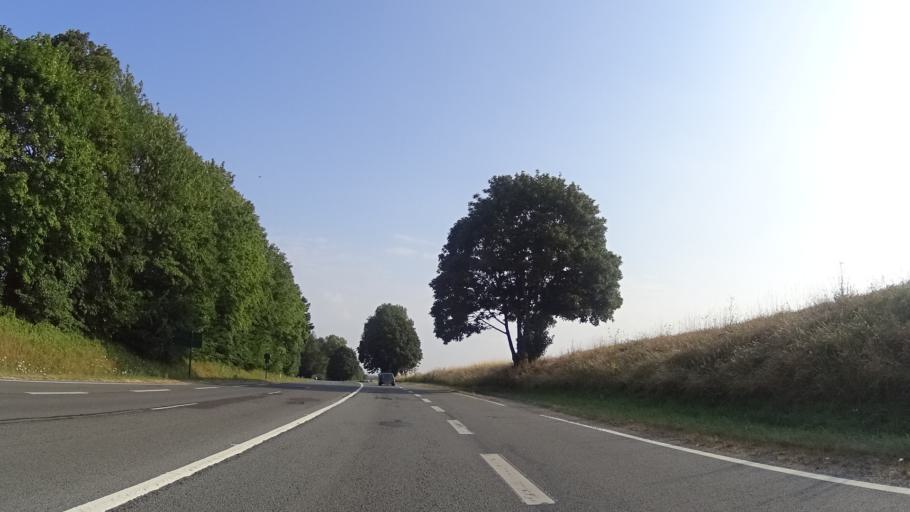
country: FR
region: Ile-de-France
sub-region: Departement du Val-d'Oise
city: Luzarches
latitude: 49.1121
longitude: 2.4305
